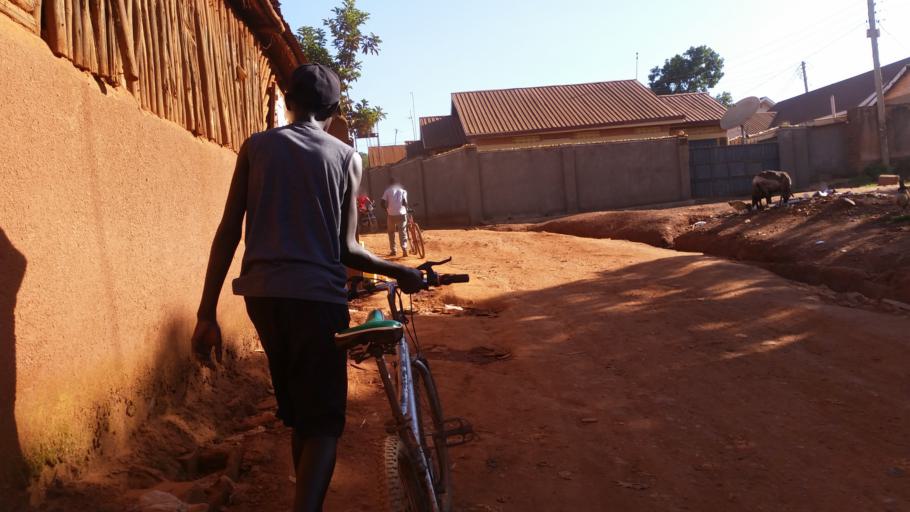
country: UG
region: Central Region
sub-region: Wakiso District
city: Kireka
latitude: 0.3238
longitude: 32.6441
